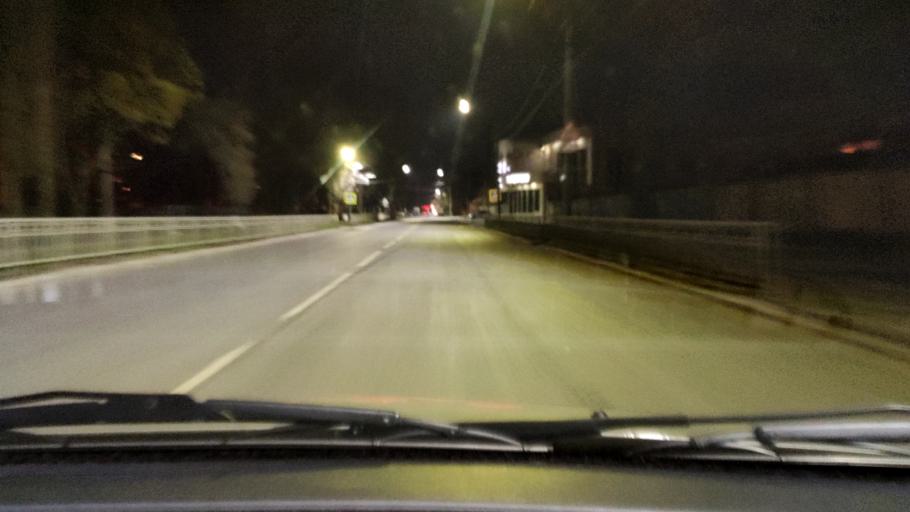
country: RU
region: Voronezj
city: Voronezh
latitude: 51.6806
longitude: 39.1940
